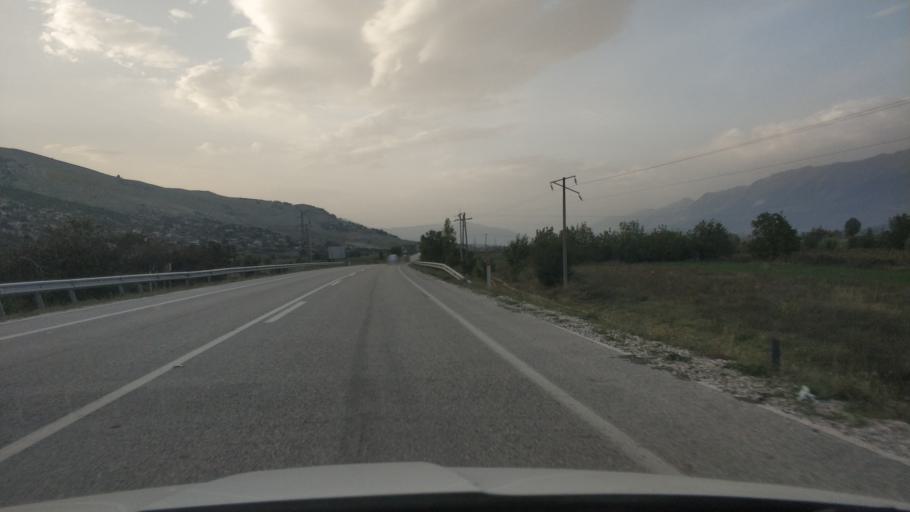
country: AL
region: Gjirokaster
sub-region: Rrethi i Gjirokastres
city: Libohove
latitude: 39.9561
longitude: 20.2496
